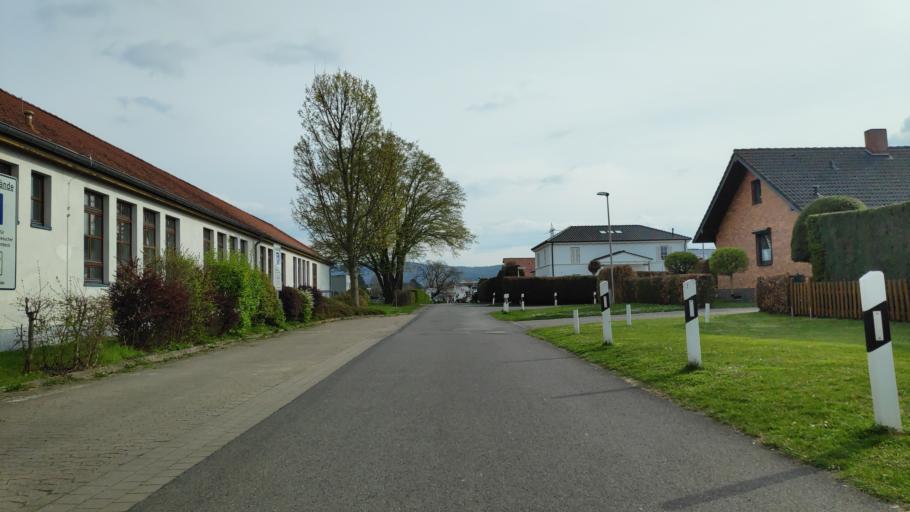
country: DE
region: North Rhine-Westphalia
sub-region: Regierungsbezirk Detmold
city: Minden
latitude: 52.2878
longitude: 8.8728
